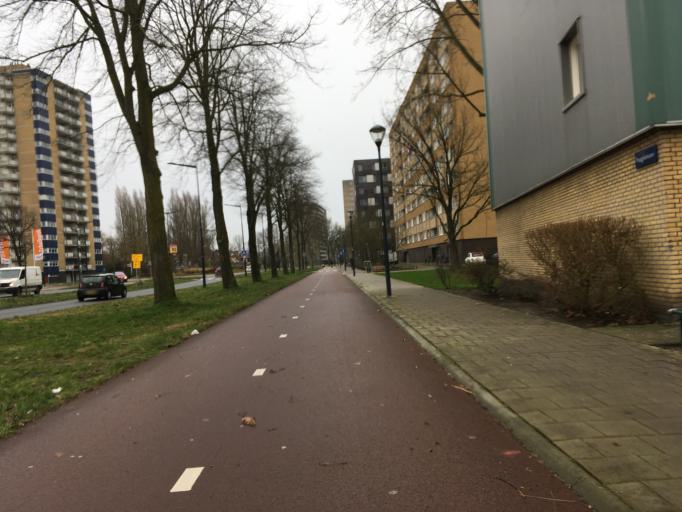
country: NL
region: North Holland
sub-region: Gemeente Haarlem
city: Haarlem
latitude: 52.3579
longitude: 4.6526
